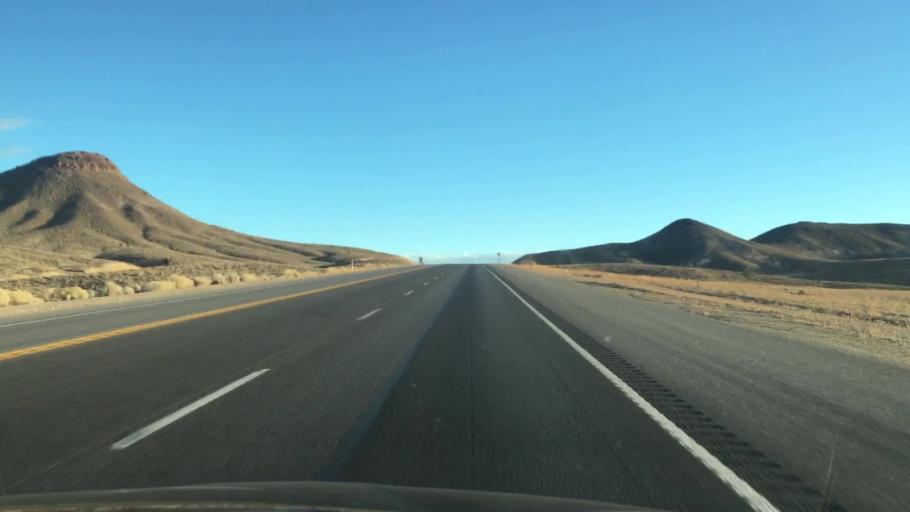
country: US
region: Nevada
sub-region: Esmeralda County
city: Goldfield
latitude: 37.6853
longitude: -117.2316
